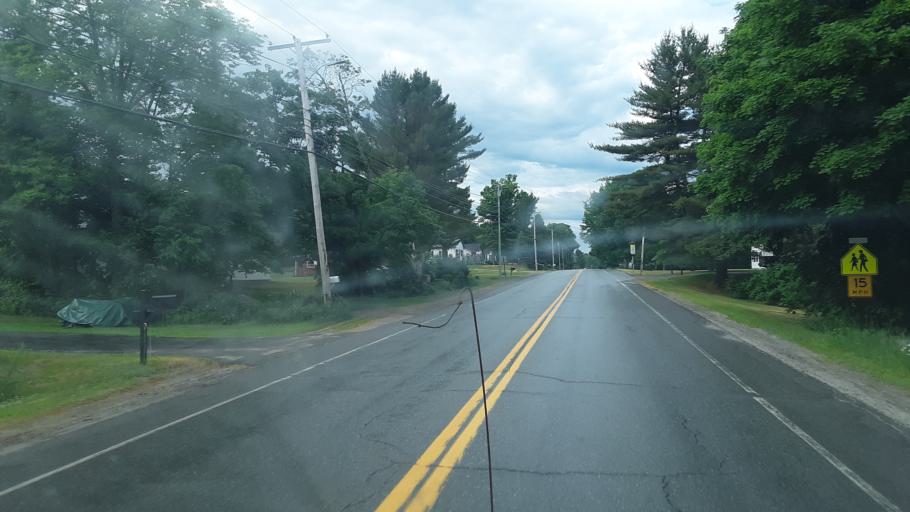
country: US
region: Maine
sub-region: Penobscot County
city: Lincoln
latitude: 45.3841
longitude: -68.4980
